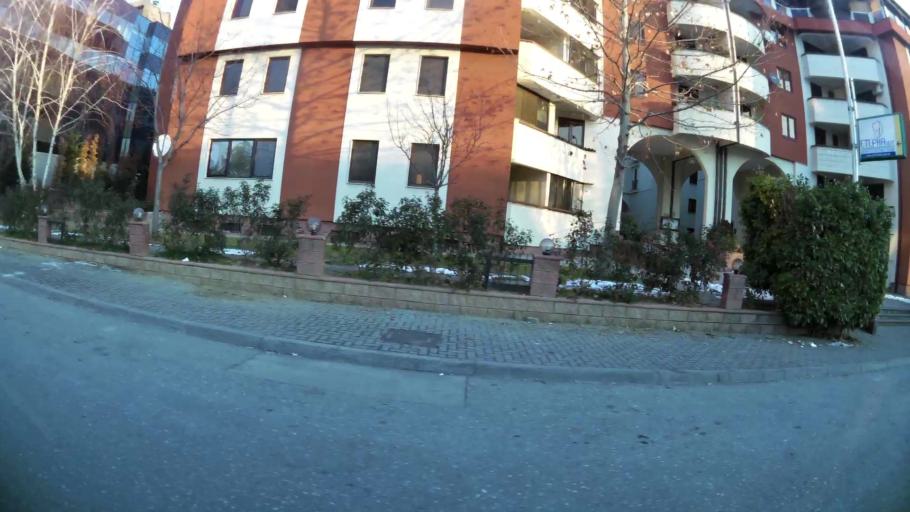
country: MK
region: Karpos
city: Skopje
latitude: 42.0057
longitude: 21.4073
